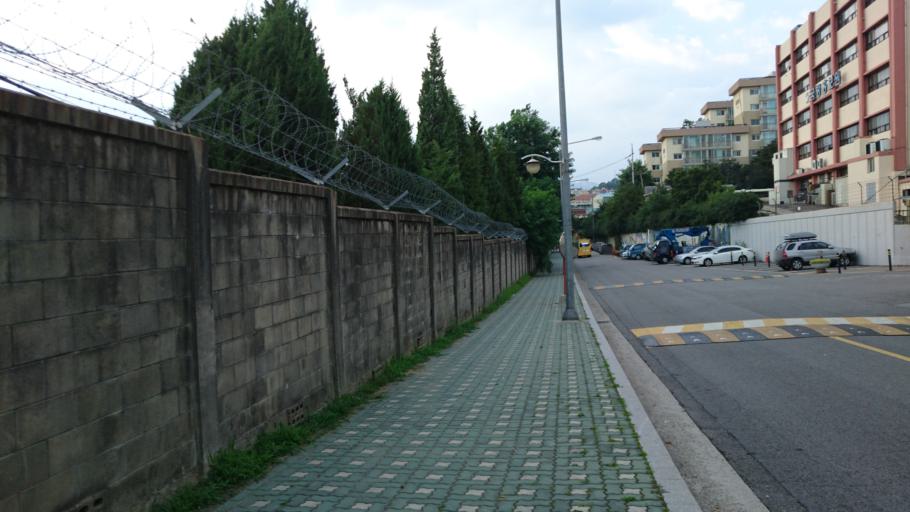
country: KR
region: Seoul
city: Seoul
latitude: 37.5426
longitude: 126.9792
